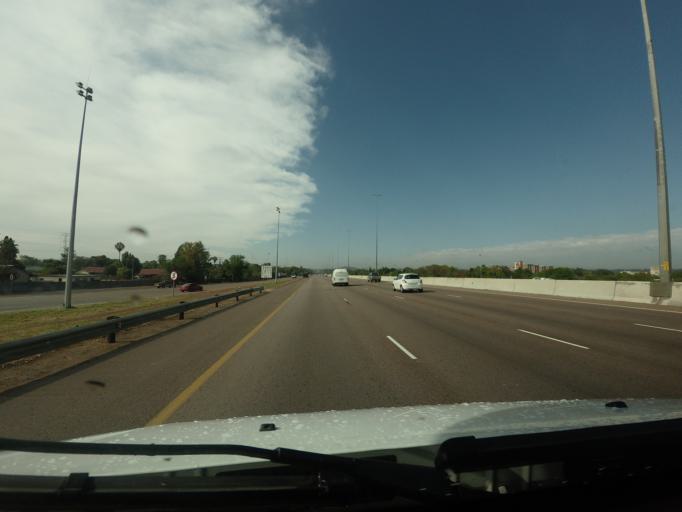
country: ZA
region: Gauteng
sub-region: City of Tshwane Metropolitan Municipality
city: Pretoria
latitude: -25.7129
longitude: 28.2658
